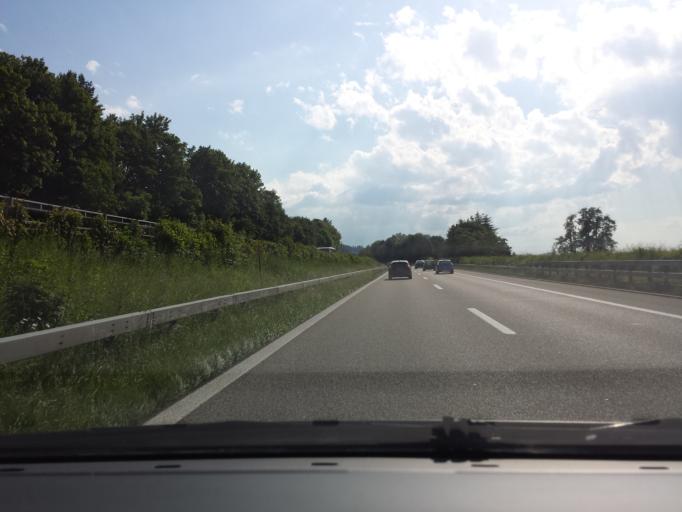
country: CH
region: Saint Gallen
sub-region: Wahlkreis Rorschach
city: Rorschach
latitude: 47.4727
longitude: 9.5168
